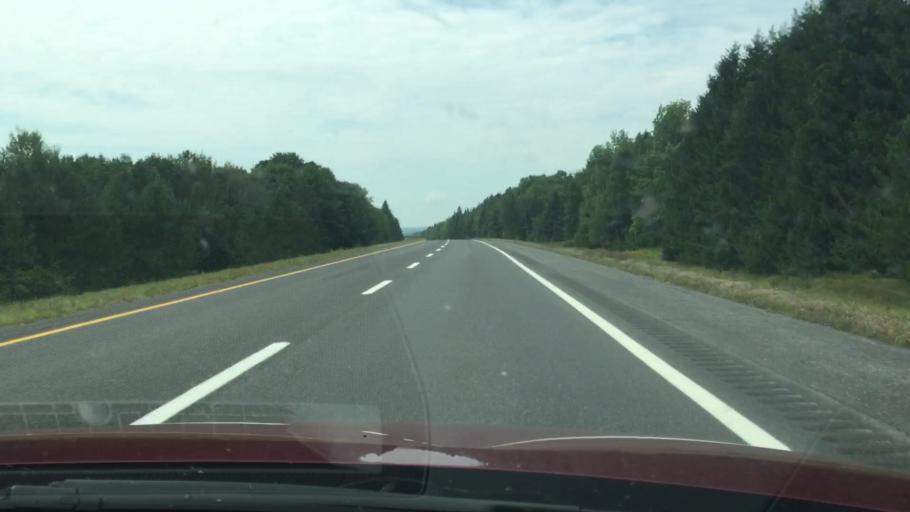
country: US
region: Maine
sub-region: Aroostook County
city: Houlton
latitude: 46.1416
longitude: -67.9403
